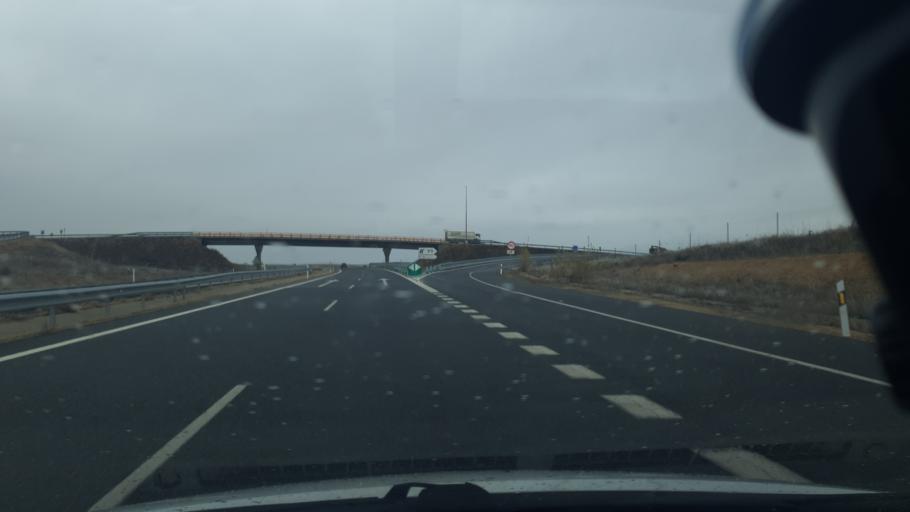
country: ES
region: Castille and Leon
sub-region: Provincia de Segovia
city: Roda de Eresma
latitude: 41.0340
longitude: -4.1907
